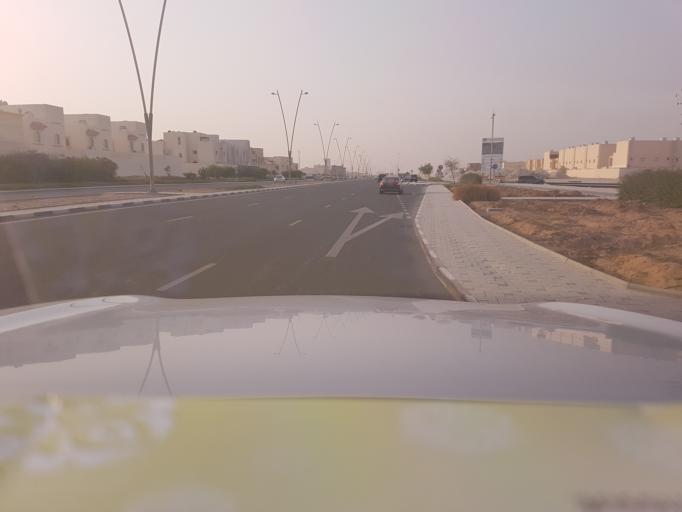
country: QA
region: Baladiyat ad Dawhah
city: Doha
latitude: 25.2293
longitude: 51.5555
